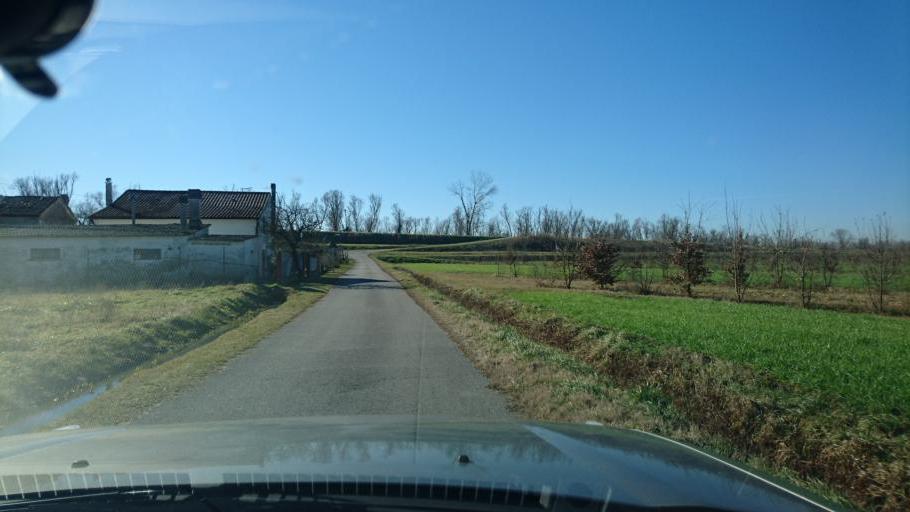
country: IT
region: Emilia-Romagna
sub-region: Provincia di Ferrara
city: Mesola
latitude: 44.9287
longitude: 12.2063
